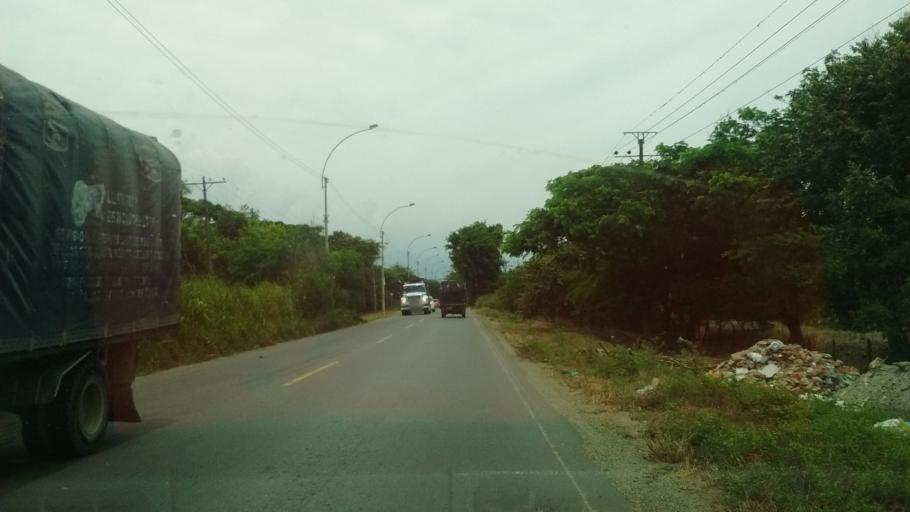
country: CO
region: Valle del Cauca
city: Jamundi
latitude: 3.3302
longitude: -76.5079
